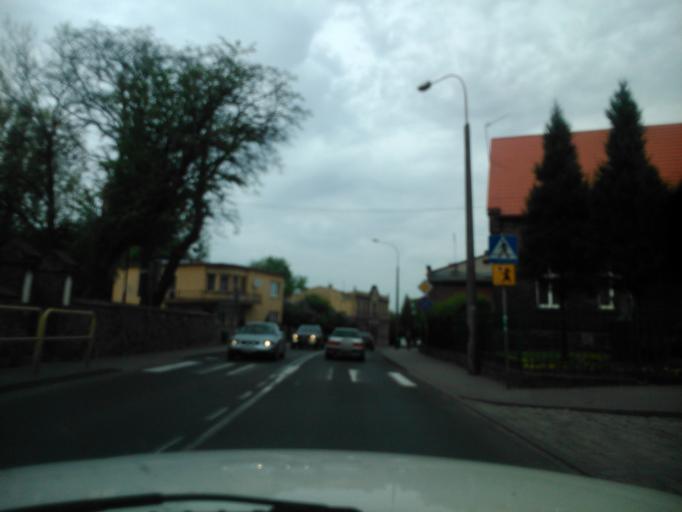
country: PL
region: Kujawsko-Pomorskie
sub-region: Powiat golubsko-dobrzynski
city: Kowalewo Pomorskie
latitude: 53.1549
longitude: 18.8980
